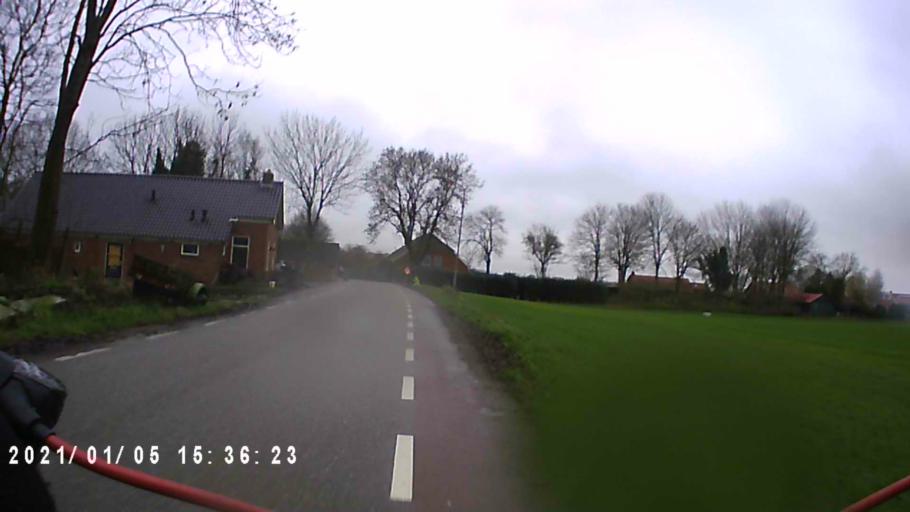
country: DE
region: Lower Saxony
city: Bunde
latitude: 53.2131
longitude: 7.1655
